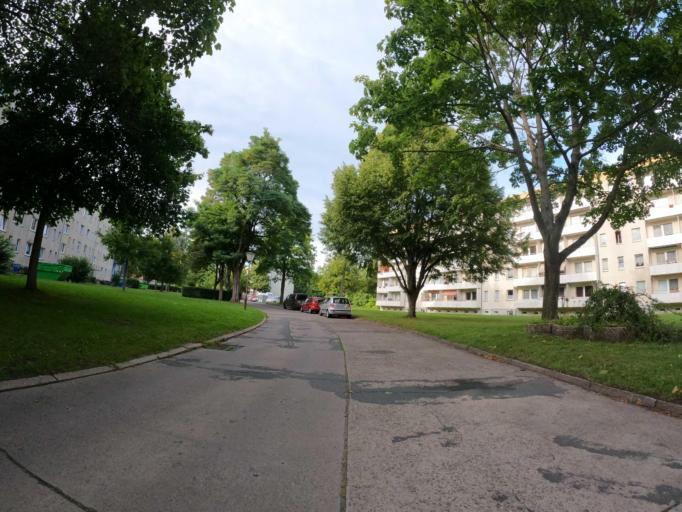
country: DE
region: Mecklenburg-Vorpommern
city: Kramerhof
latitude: 54.3290
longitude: 13.0586
